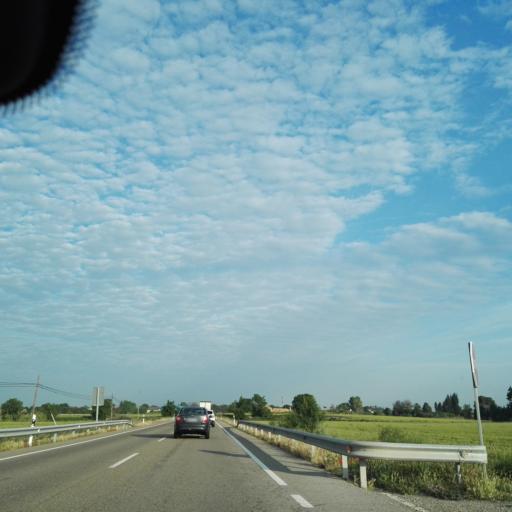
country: ES
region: Aragon
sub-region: Provincia de Zaragoza
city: Oliver-Valdefierro, Oliver, Valdefierro
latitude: 41.6618
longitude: -0.9570
